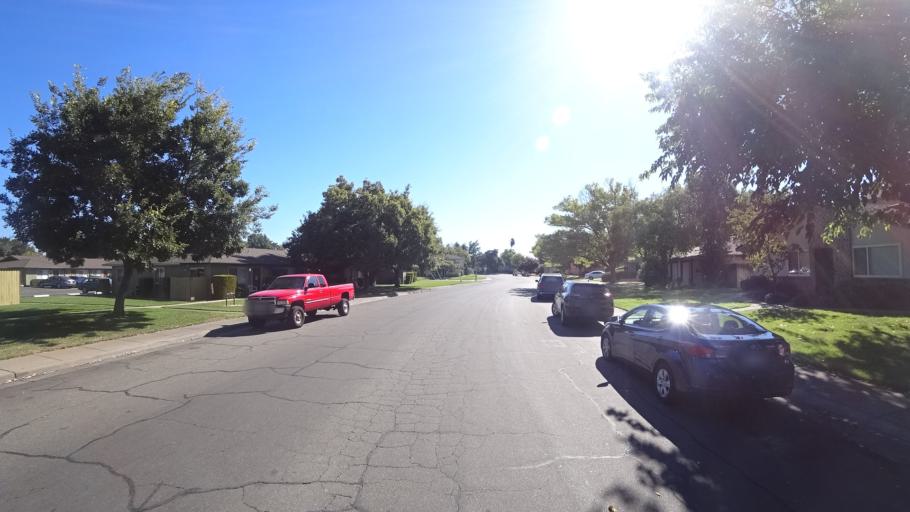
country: US
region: California
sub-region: Sacramento County
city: Elk Grove
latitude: 38.4057
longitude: -121.3680
